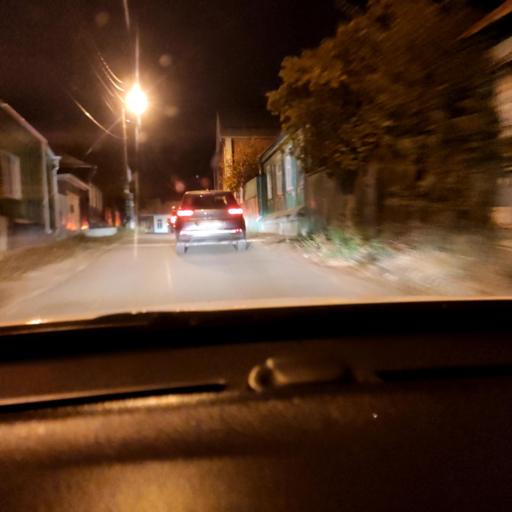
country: RU
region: Voronezj
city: Voronezh
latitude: 51.6890
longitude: 39.2245
